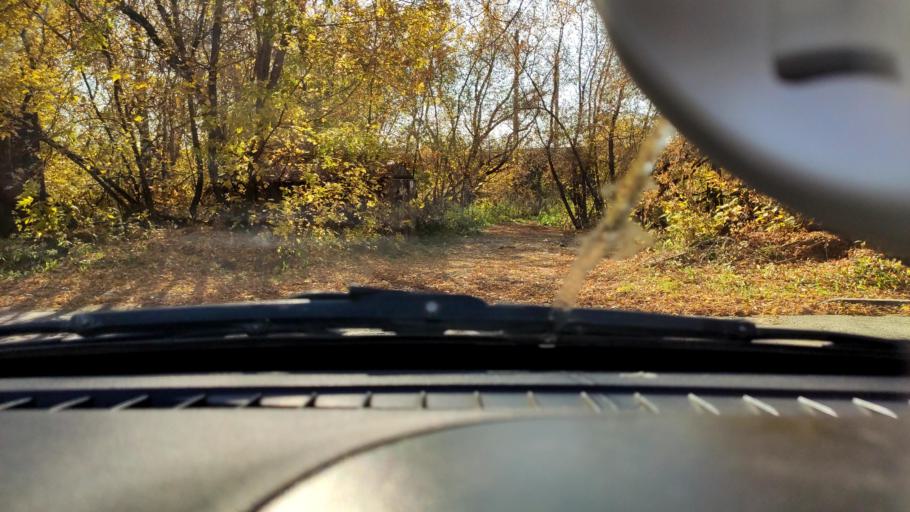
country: RU
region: Perm
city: Kondratovo
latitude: 58.0408
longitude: 56.0980
